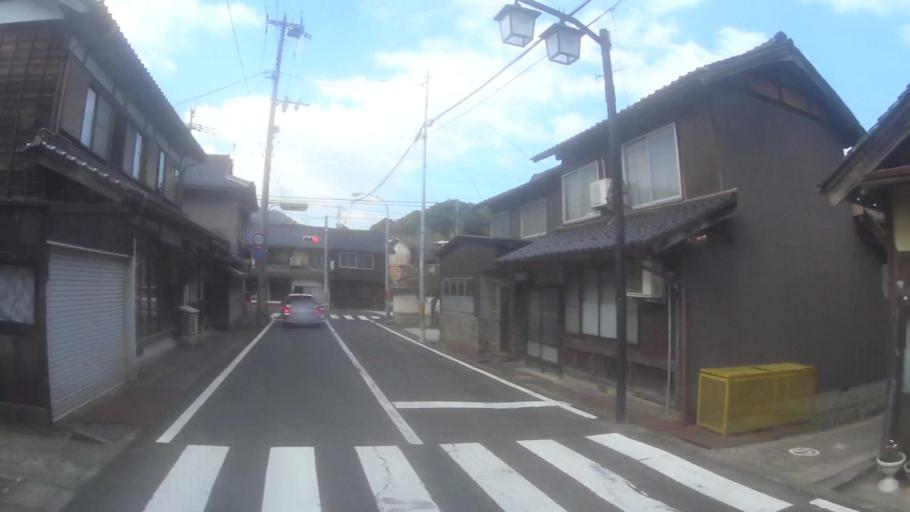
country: JP
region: Kyoto
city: Miyazu
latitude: 35.5816
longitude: 135.0933
